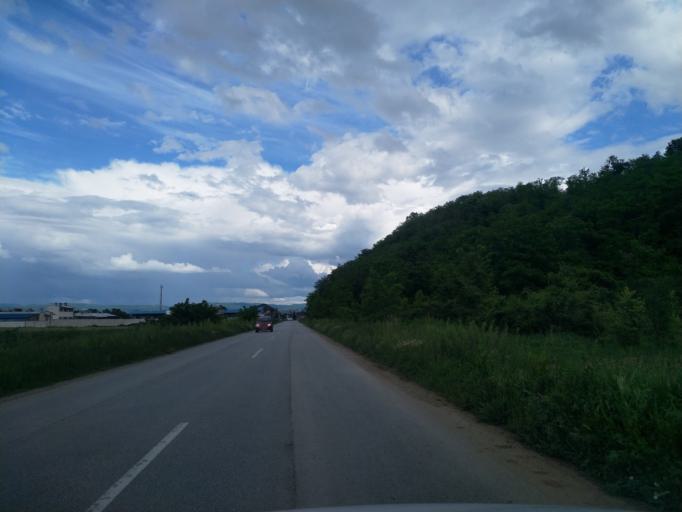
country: RS
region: Central Serbia
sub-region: Pomoravski Okrug
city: Jagodina
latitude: 43.9544
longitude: 21.3115
